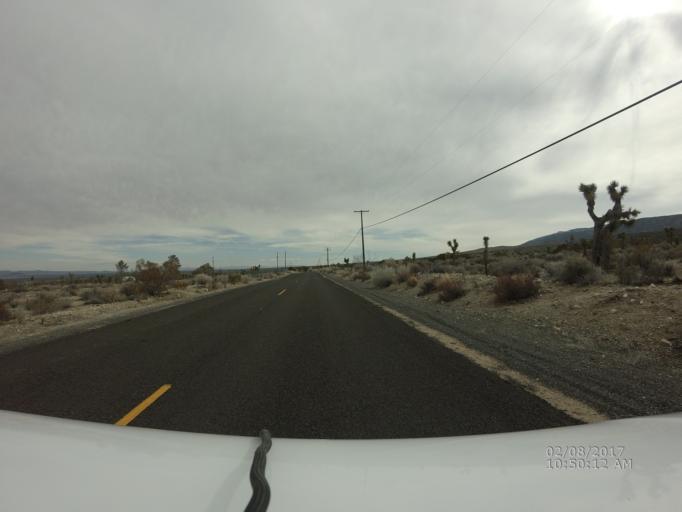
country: US
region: California
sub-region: San Bernardino County
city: Pinon Hills
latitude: 34.4694
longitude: -117.7601
